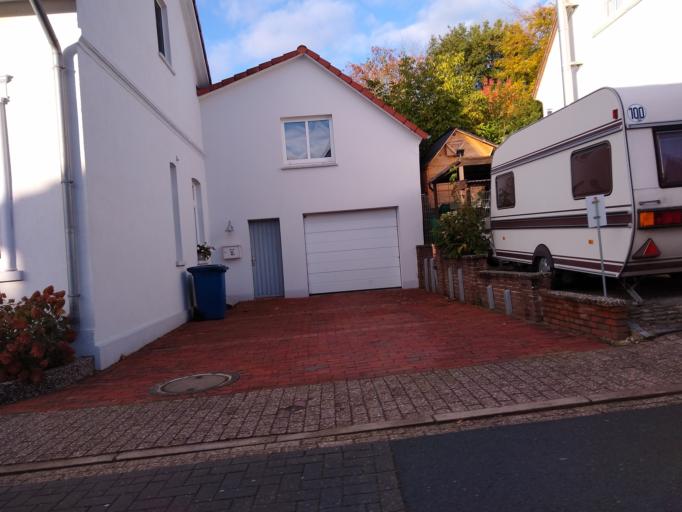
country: DE
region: Lower Saxony
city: Rastede
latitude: 53.2432
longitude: 8.1978
